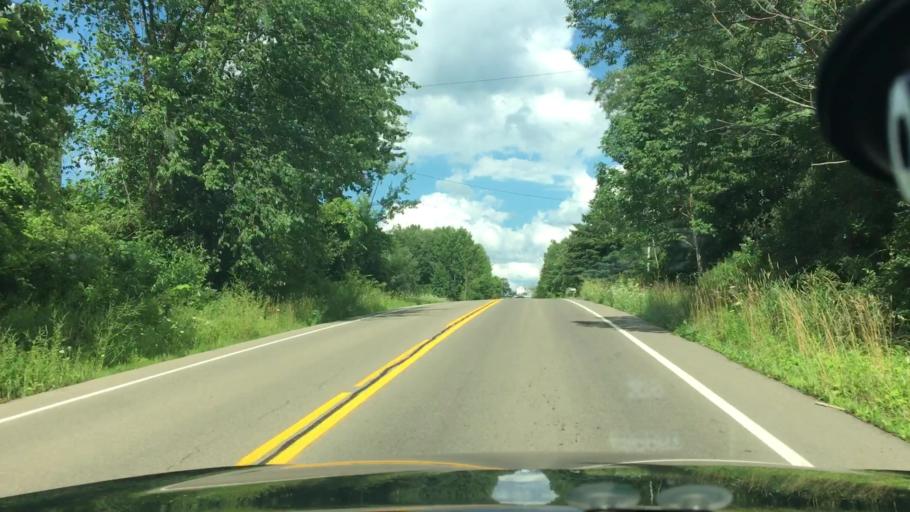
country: US
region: New York
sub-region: Chautauqua County
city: Lakewood
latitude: 42.1799
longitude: -79.3548
